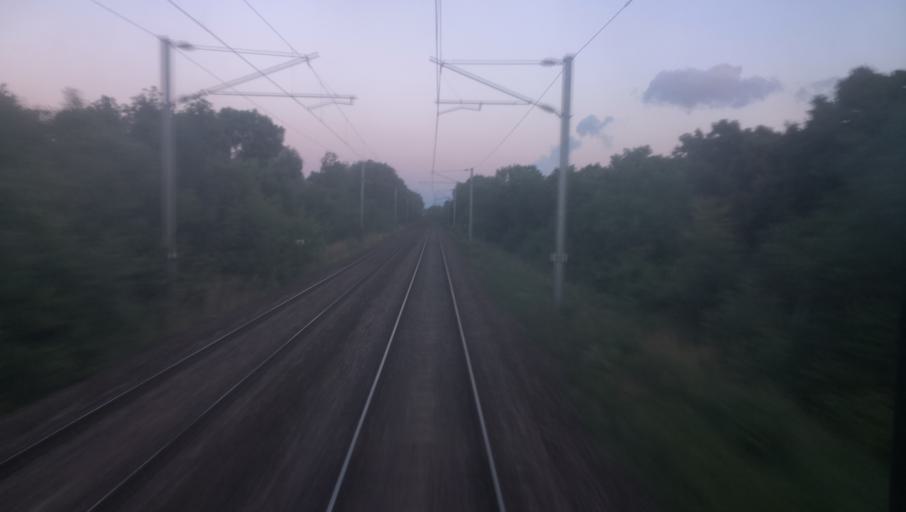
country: FR
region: Centre
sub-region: Departement du Loiret
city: Bonny-sur-Loire
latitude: 47.5505
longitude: 2.8514
